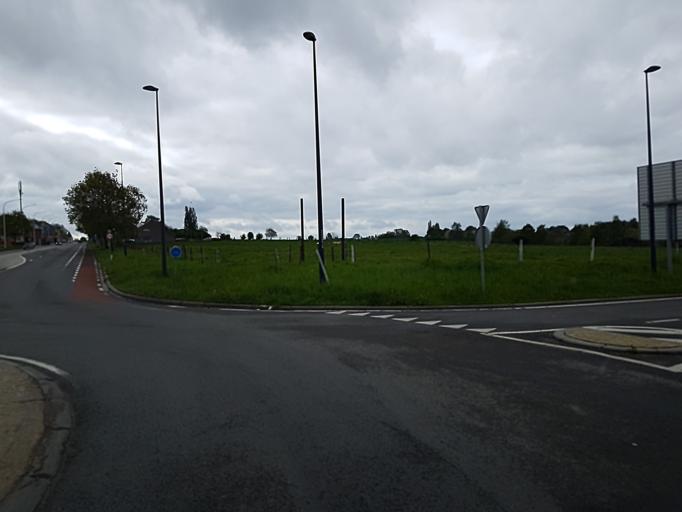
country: BE
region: Wallonia
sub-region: Province du Brabant Wallon
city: Chastre-Villeroux-Blanmont
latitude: 50.6322
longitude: 4.6534
